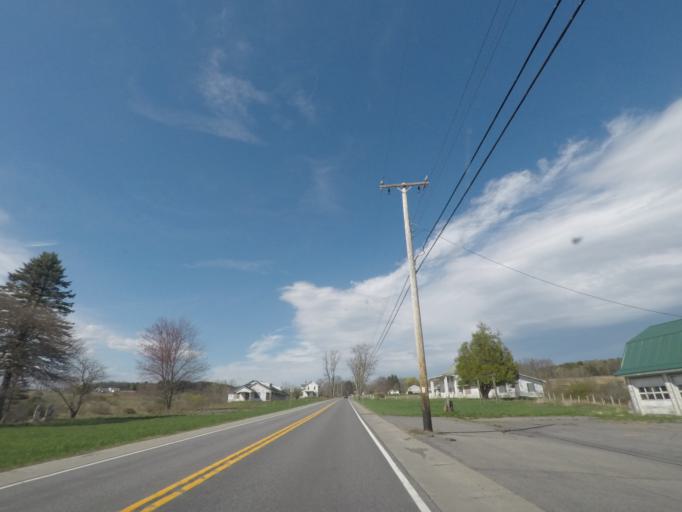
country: US
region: New York
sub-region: Greene County
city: Cairo
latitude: 42.4437
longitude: -74.0158
